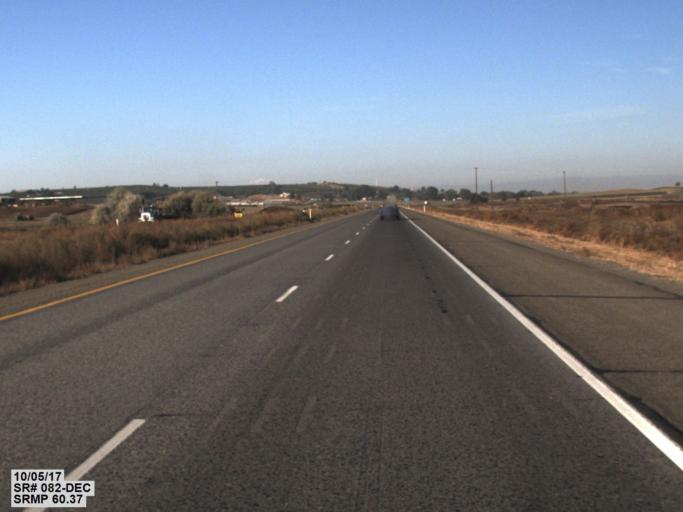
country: US
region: Washington
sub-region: Yakima County
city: Granger
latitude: 46.3386
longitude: -120.1424
